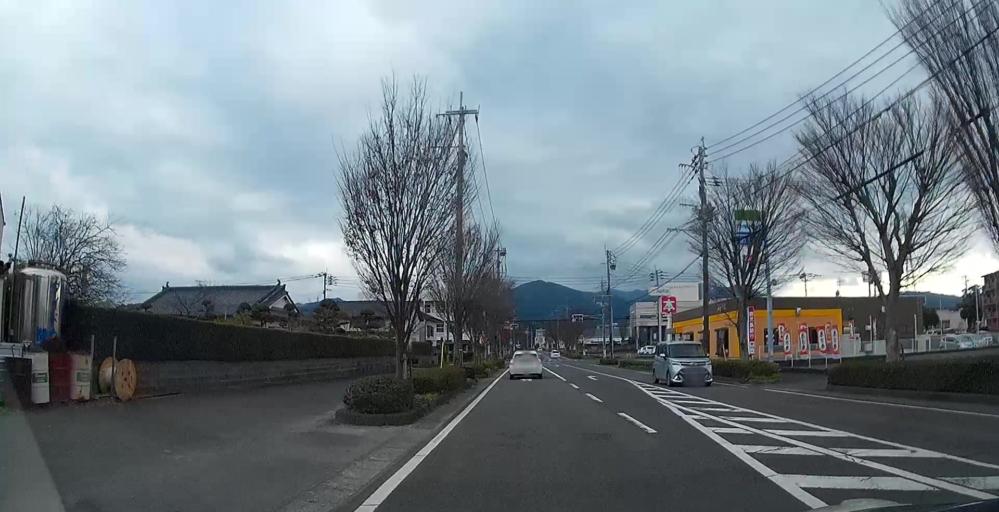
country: JP
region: Kagoshima
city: Izumi
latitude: 32.0750
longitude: 130.3477
